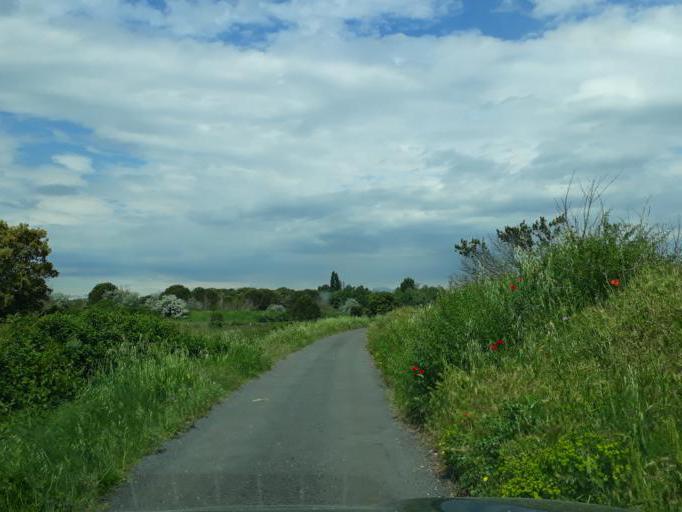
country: FR
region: Languedoc-Roussillon
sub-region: Departement de l'Herault
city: Agde
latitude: 43.2906
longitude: 3.4884
